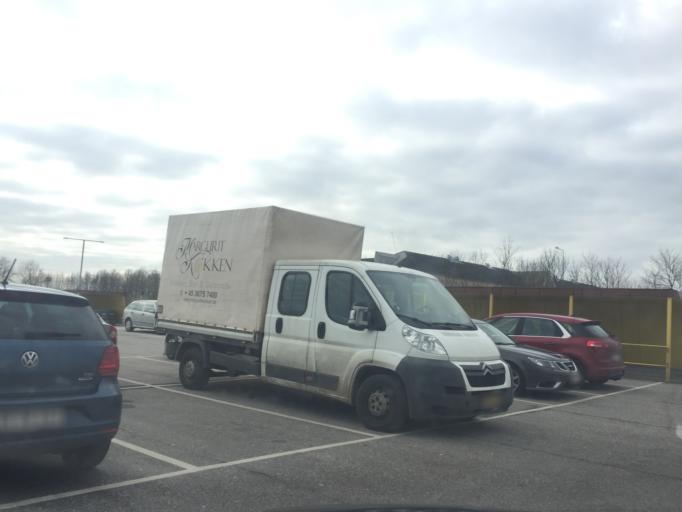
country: DK
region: Capital Region
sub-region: Hoje-Taastrup Kommune
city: Taastrup
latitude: 55.6435
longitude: 12.2741
